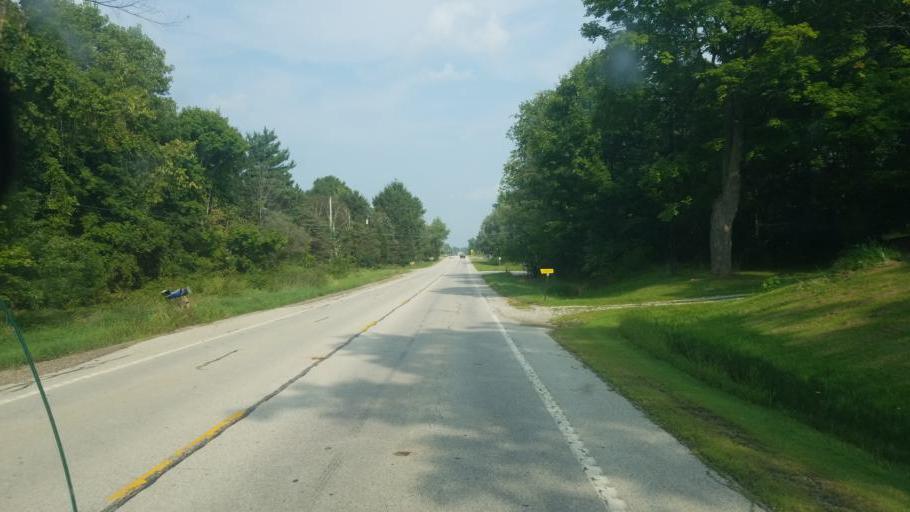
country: US
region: Ohio
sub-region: Medina County
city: Medina
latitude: 41.1675
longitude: -81.9658
